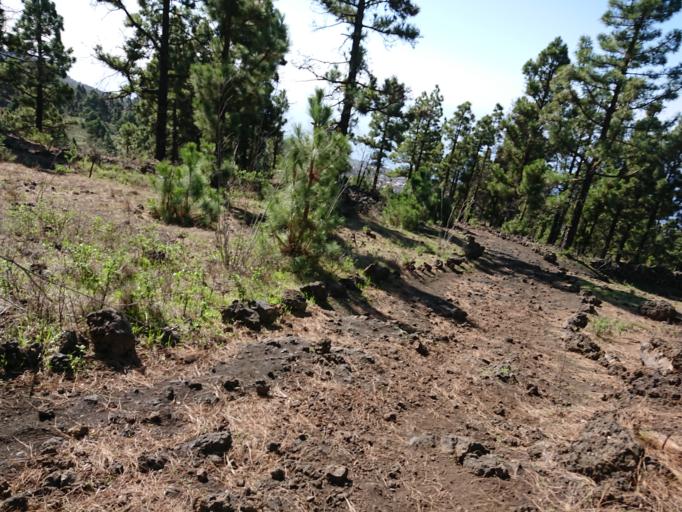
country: ES
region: Canary Islands
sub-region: Provincia de Santa Cruz de Tenerife
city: El Paso
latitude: 28.6079
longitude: -17.8662
